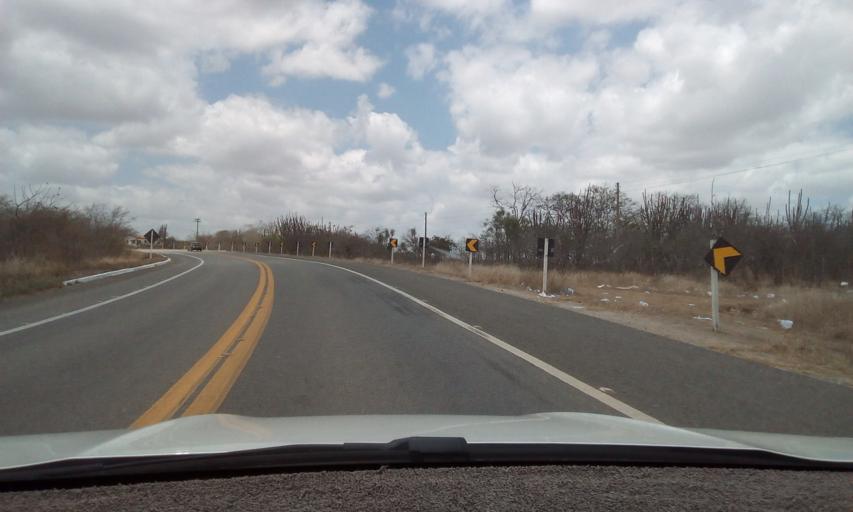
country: BR
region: Paraiba
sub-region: Boqueirao
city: Boqueirao
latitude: -7.5917
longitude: -36.0427
